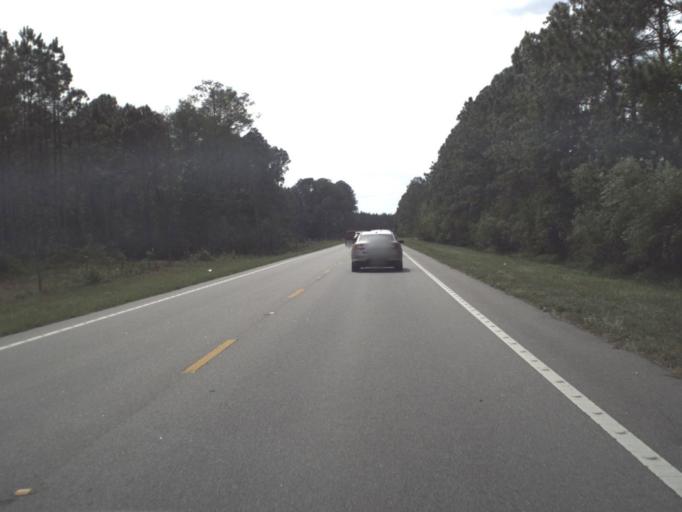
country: US
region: Florida
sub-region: Putnam County
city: Crescent City
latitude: 29.4806
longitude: -81.4412
